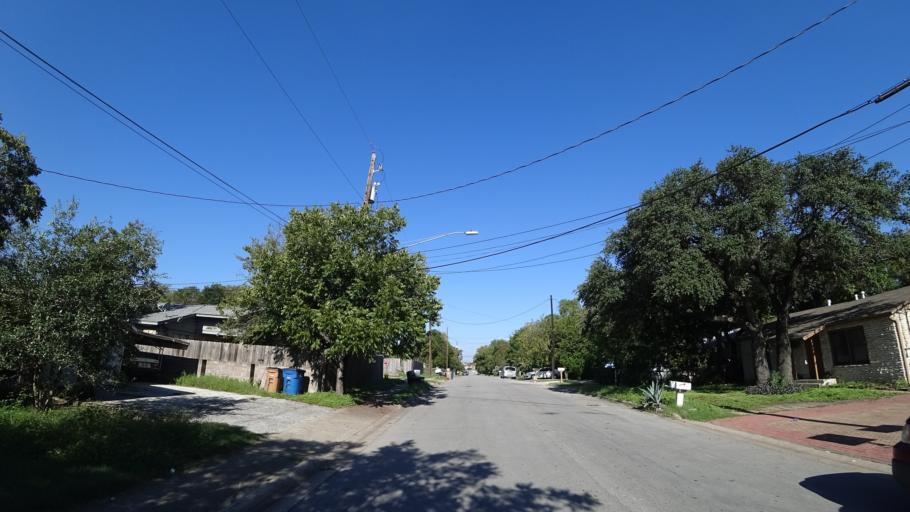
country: US
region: Texas
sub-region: Travis County
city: Austin
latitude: 30.3523
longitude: -97.7002
